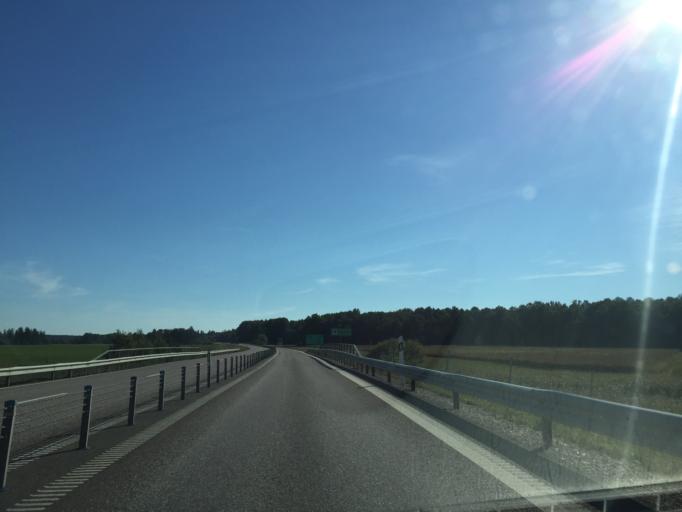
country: SE
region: Vaestmanland
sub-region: Arboga Kommun
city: Arboga
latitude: 59.4241
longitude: 15.8886
